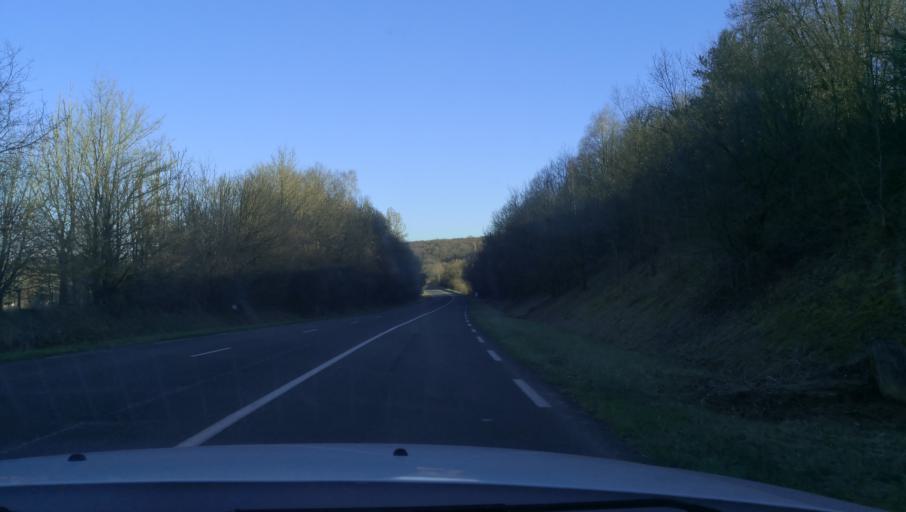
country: FR
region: Haute-Normandie
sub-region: Departement de la Seine-Maritime
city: Saint-Saens
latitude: 49.6540
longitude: 1.2873
